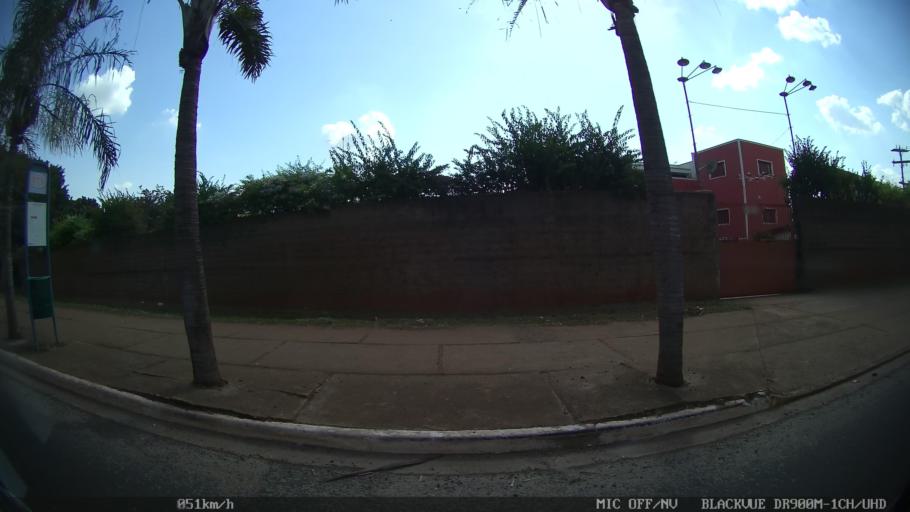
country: BR
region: Sao Paulo
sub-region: Ribeirao Preto
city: Ribeirao Preto
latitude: -21.1841
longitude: -47.8422
